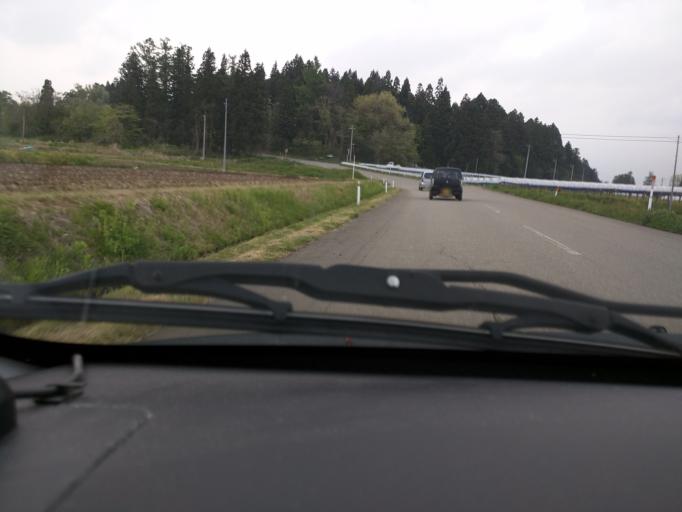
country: JP
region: Fukushima
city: Kitakata
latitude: 37.4981
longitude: 139.8208
